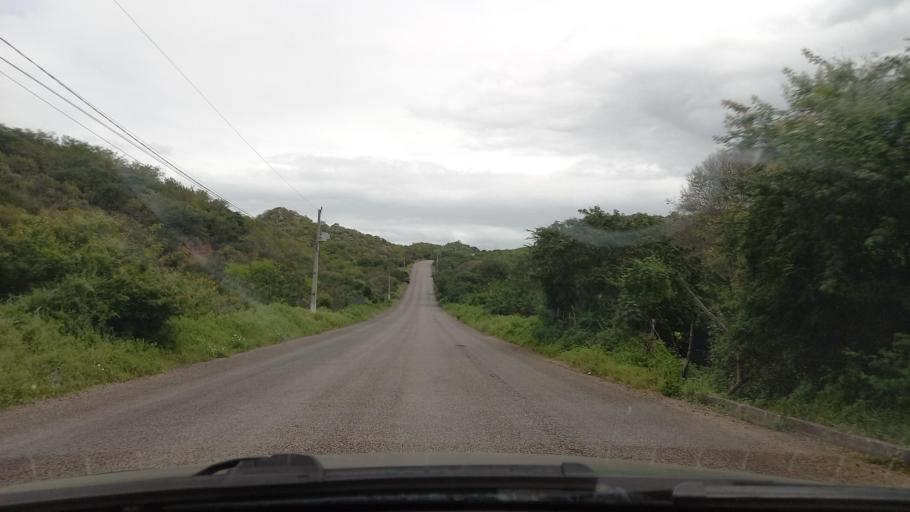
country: BR
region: Sergipe
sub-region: Caninde De Sao Francisco
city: Caninde de Sao Francisco
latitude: -9.6326
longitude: -37.7775
